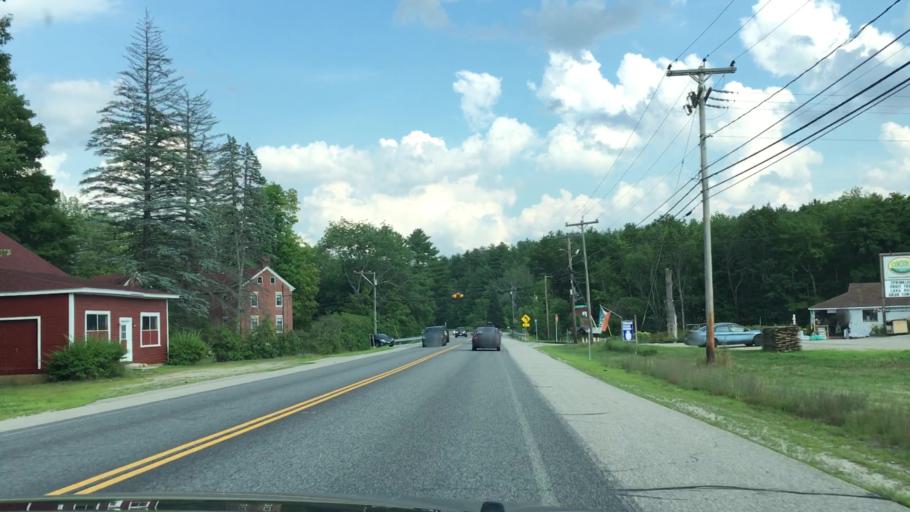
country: US
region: New Hampshire
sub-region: Strafford County
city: Farmington
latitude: 43.3876
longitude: -71.0831
